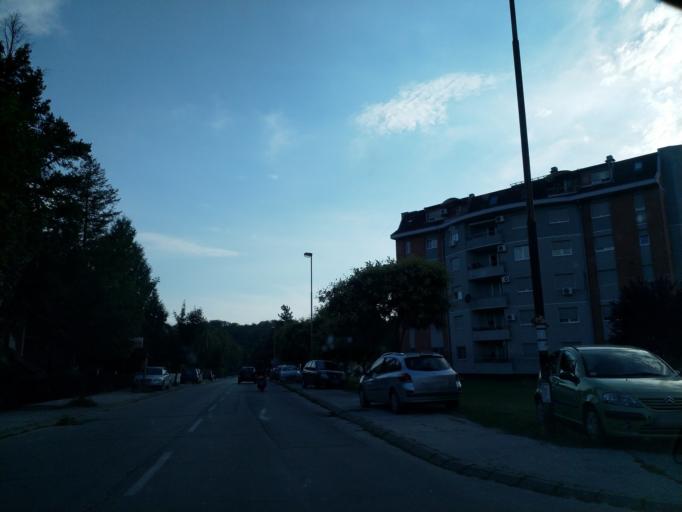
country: RS
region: Central Serbia
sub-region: Pomoravski Okrug
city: Jagodina
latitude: 43.9856
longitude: 21.2446
